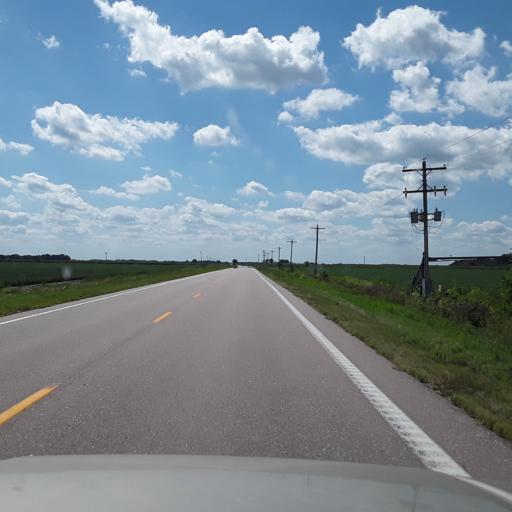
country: US
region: Nebraska
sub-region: Merrick County
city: Central City
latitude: 41.1913
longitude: -98.0533
